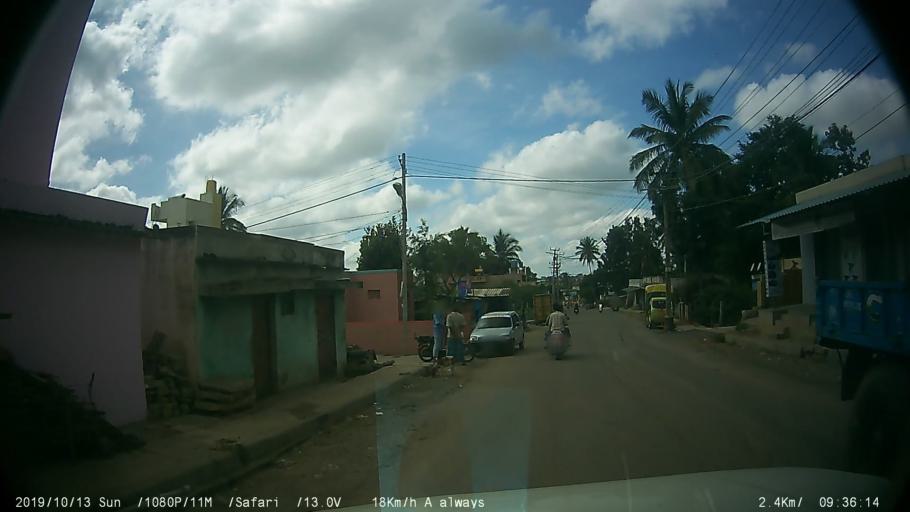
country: IN
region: Karnataka
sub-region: Bangalore Urban
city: Anekal
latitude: 12.8063
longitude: 77.6270
